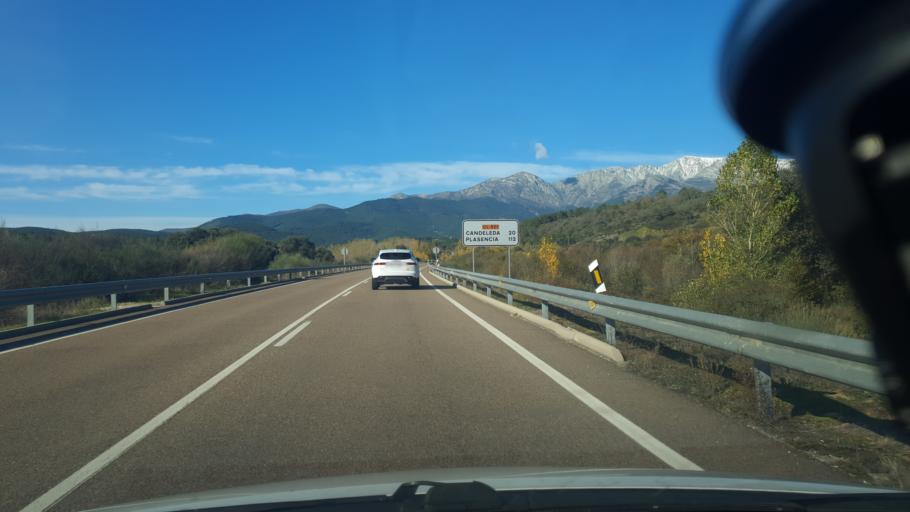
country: ES
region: Castille and Leon
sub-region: Provincia de Avila
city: Arenas de San Pedro
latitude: 40.1864
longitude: -5.0576
